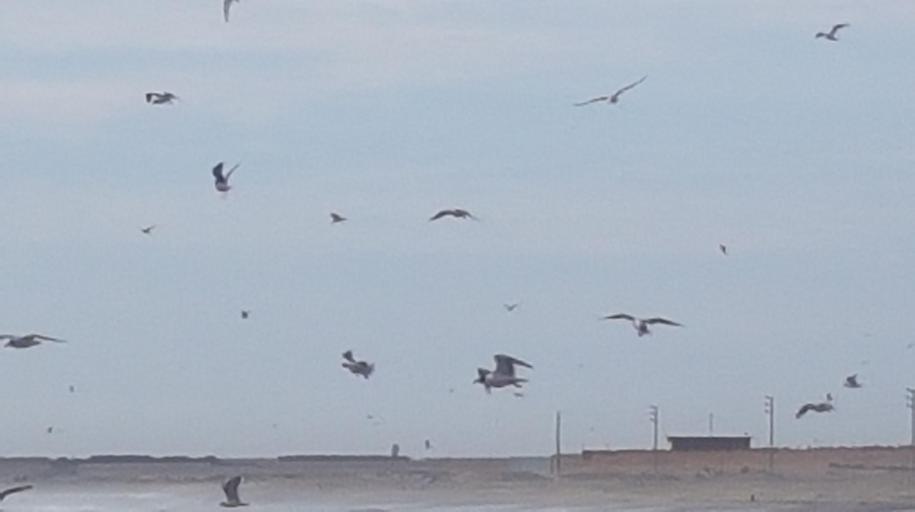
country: PE
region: Ancash
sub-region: Provincia de Santa
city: Coishco
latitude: -9.0155
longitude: -78.6233
